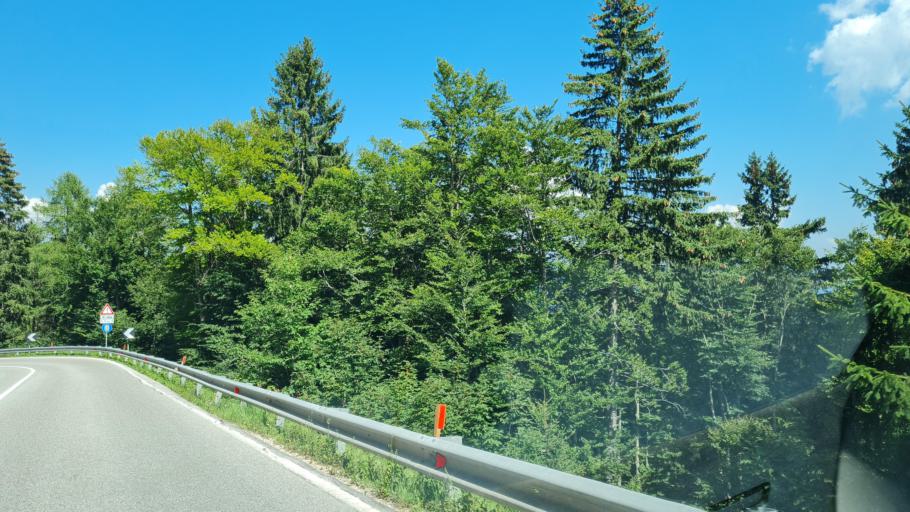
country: IT
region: Trentino-Alto Adige
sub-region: Provincia di Trento
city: Folgaria
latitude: 45.9203
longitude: 11.2072
